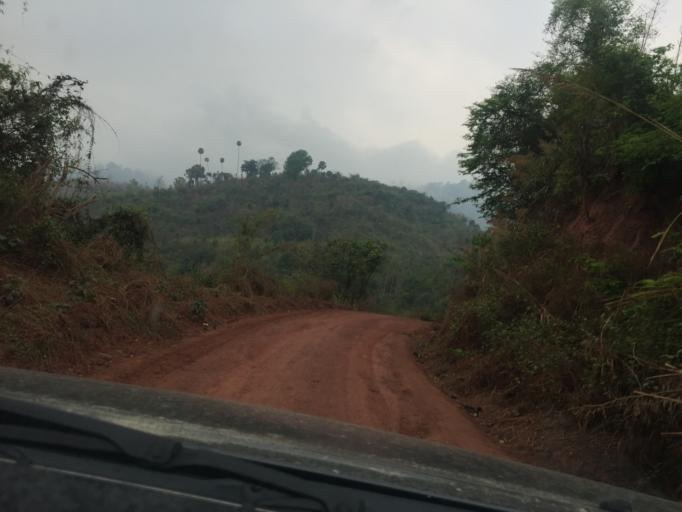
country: TH
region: Nan
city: Bo Kluea
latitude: 18.8470
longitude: 101.4137
